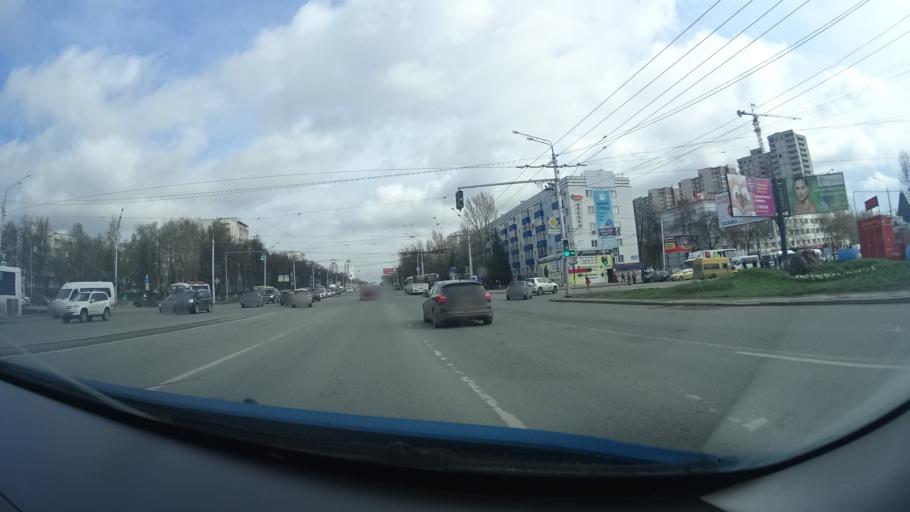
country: RU
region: Bashkortostan
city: Ufa
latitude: 54.7551
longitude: 56.0009
